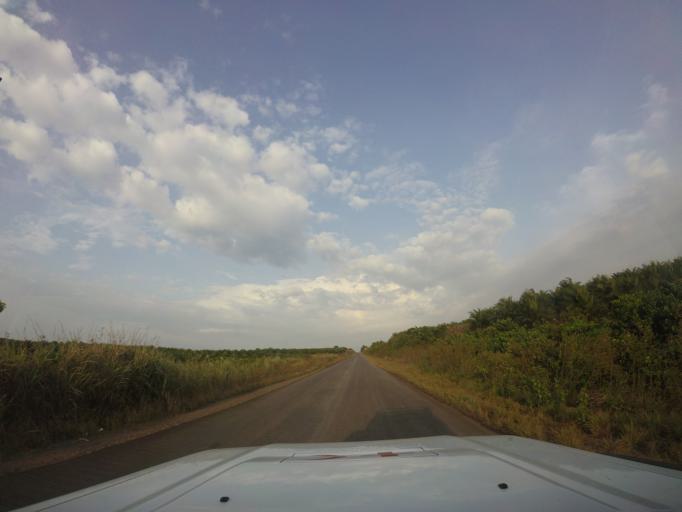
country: LR
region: Bomi
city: Tubmanburg
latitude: 6.7267
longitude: -11.0426
